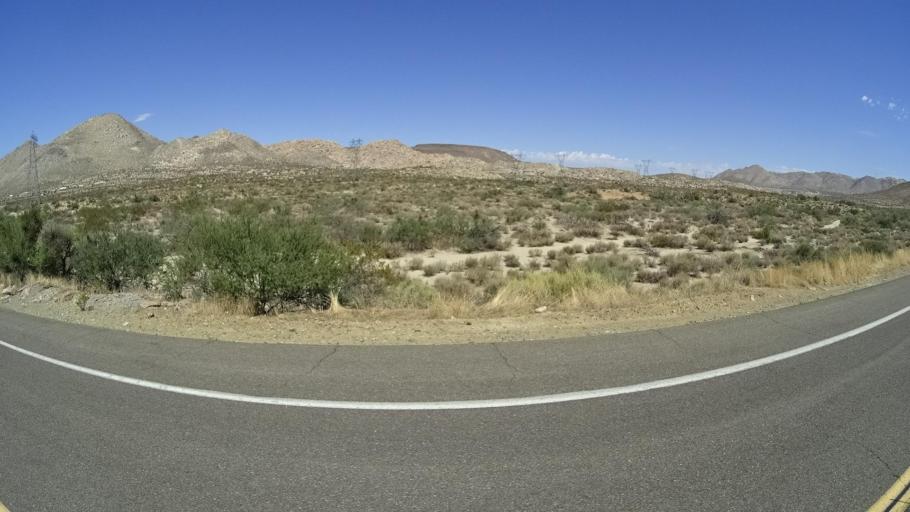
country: MX
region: Baja California
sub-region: Tecate
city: Cereso del Hongo
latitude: 32.6271
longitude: -116.1619
